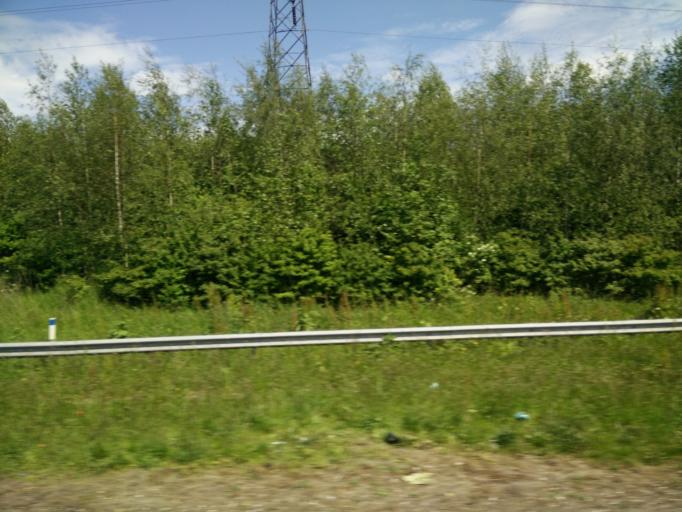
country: GB
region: England
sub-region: Hertfordshire
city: Flamstead
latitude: 51.8240
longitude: -0.4174
